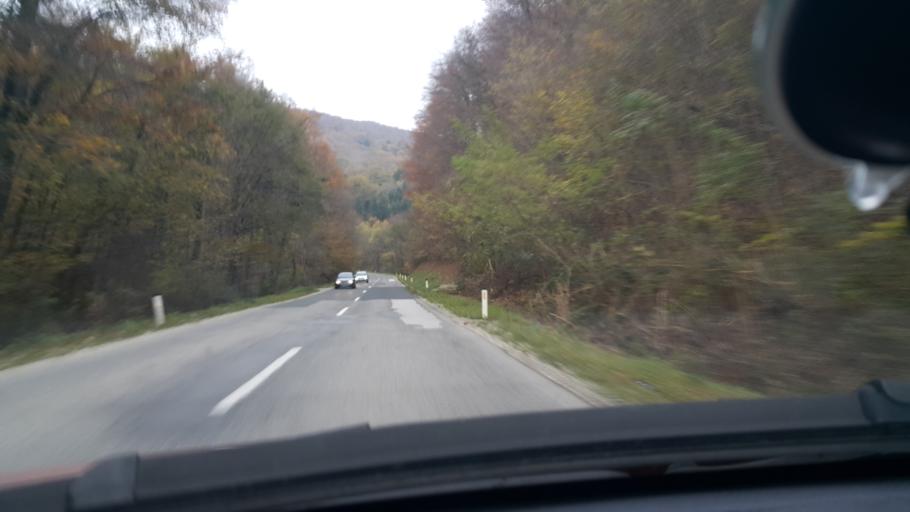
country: SI
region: Bistrica ob Sotli
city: Bistrica ob Sotli
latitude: 46.0397
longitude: 15.6871
